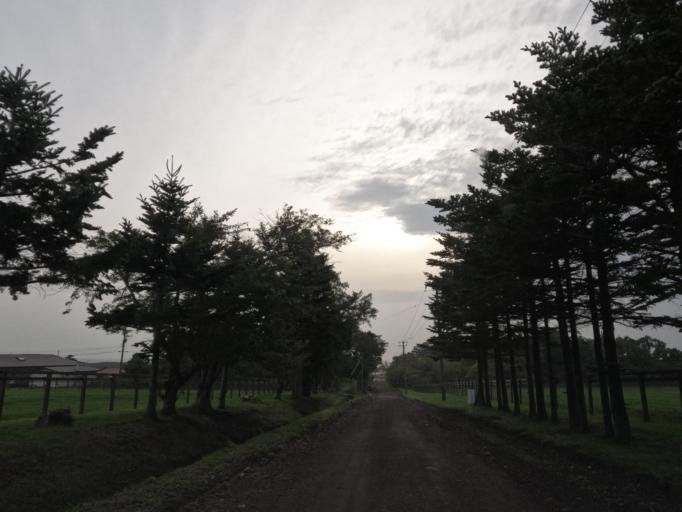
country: JP
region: Hokkaido
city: Date
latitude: 42.4231
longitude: 140.9130
